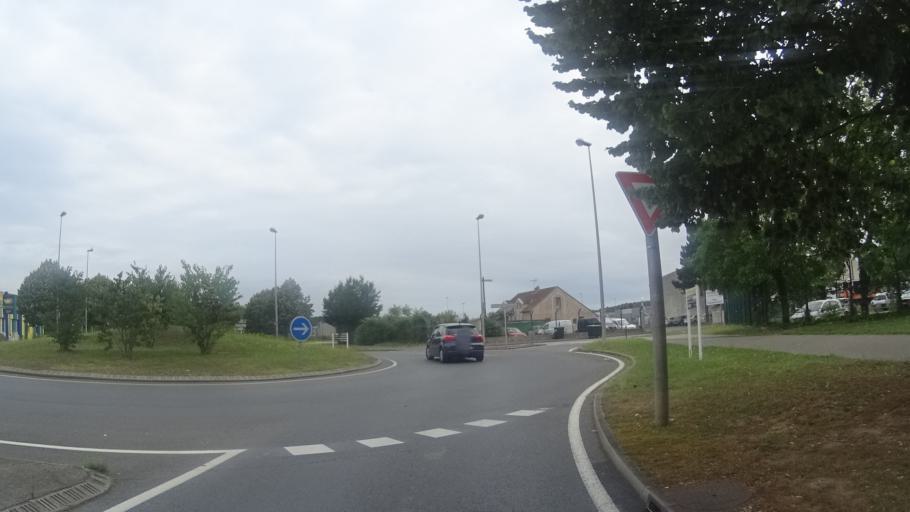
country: FR
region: Aquitaine
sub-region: Departement de la Dordogne
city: Chancelade
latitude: 45.1908
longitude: 0.6617
